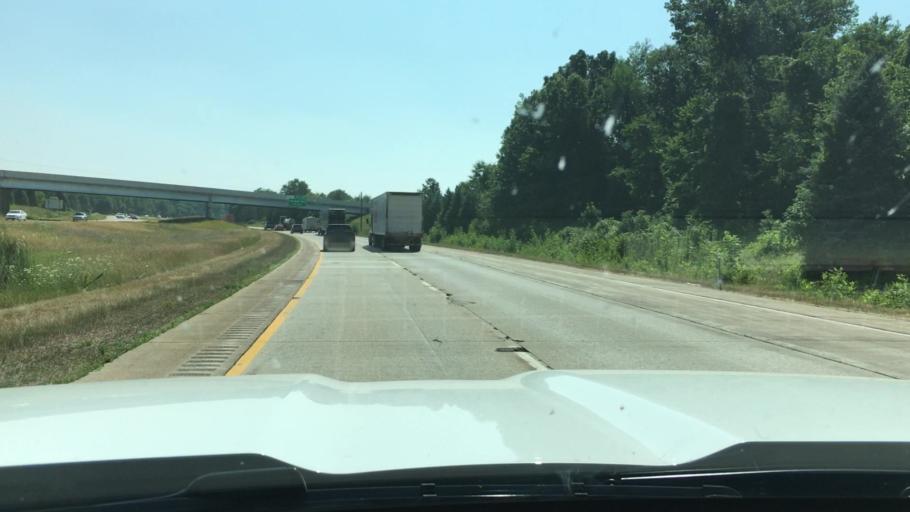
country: US
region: Michigan
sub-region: Clinton County
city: DeWitt
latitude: 42.8146
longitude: -84.5797
